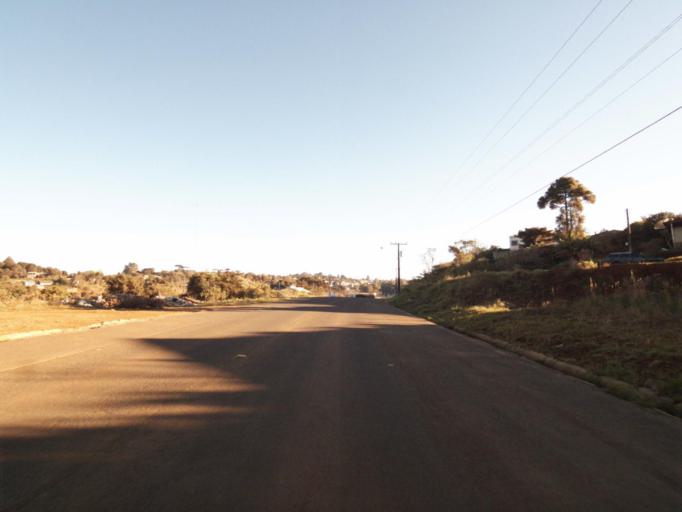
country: AR
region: Misiones
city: Bernardo de Irigoyen
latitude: -26.2638
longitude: -53.6403
